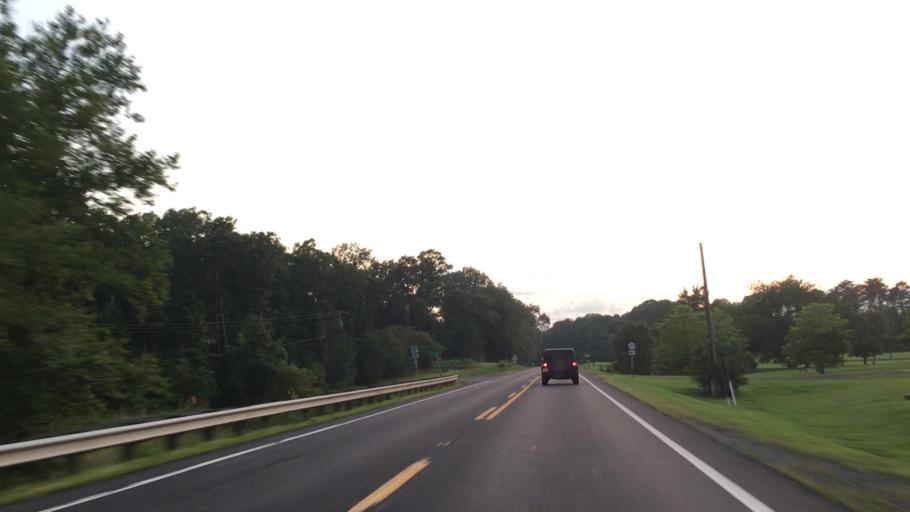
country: US
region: Virginia
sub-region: Orange County
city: Orange
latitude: 38.2618
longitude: -77.9838
